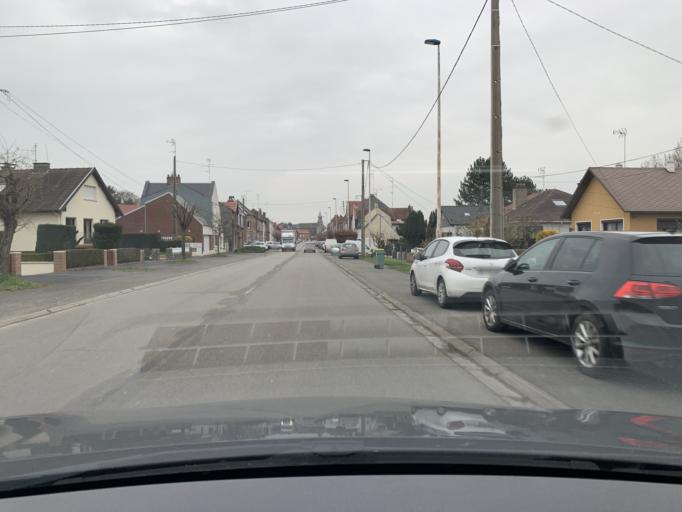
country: FR
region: Nord-Pas-de-Calais
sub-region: Departement du Nord
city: Proville
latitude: 50.1770
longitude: 3.2083
